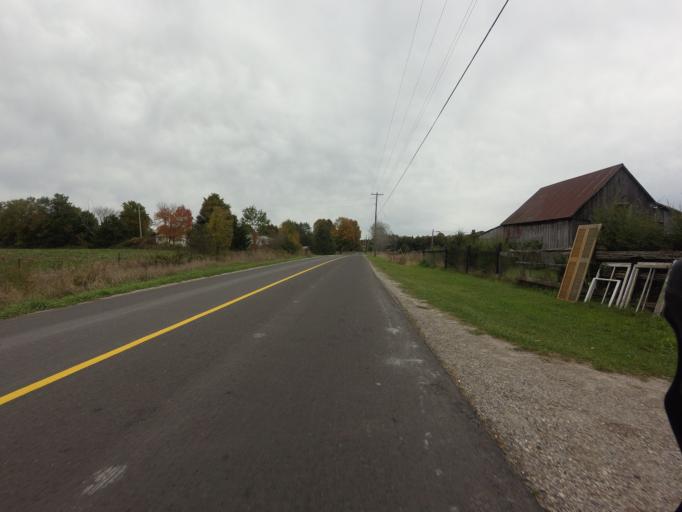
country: CA
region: Ontario
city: Gananoque
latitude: 44.5814
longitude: -76.0726
